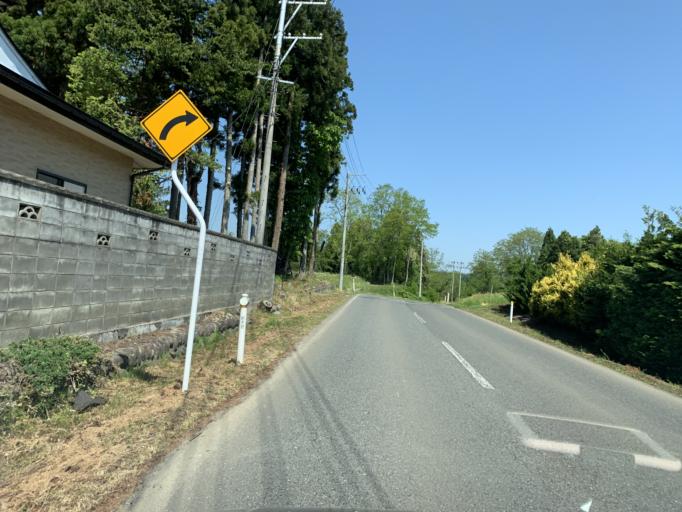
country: JP
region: Iwate
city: Mizusawa
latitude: 39.1661
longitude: 141.0626
